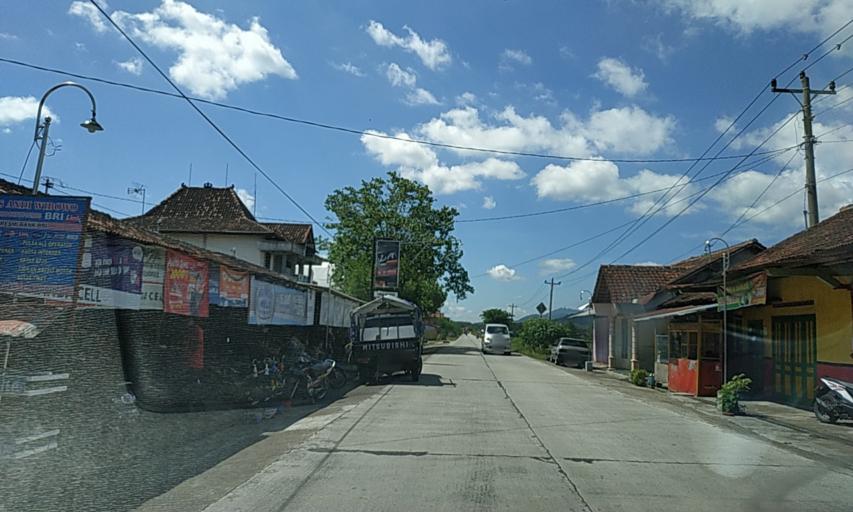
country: ID
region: Central Java
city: Trucuk
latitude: -7.7384
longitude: 110.7419
